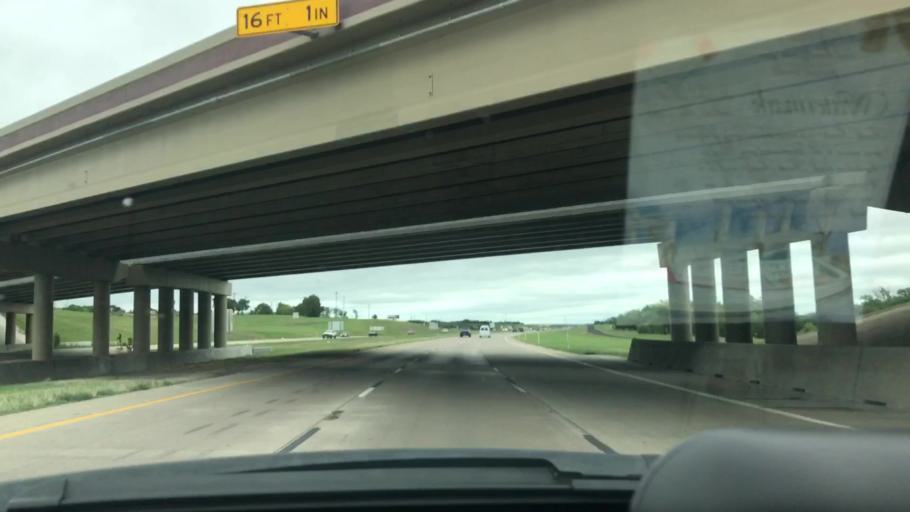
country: US
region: Texas
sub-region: Grayson County
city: Sherman
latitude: 33.6806
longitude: -96.6078
